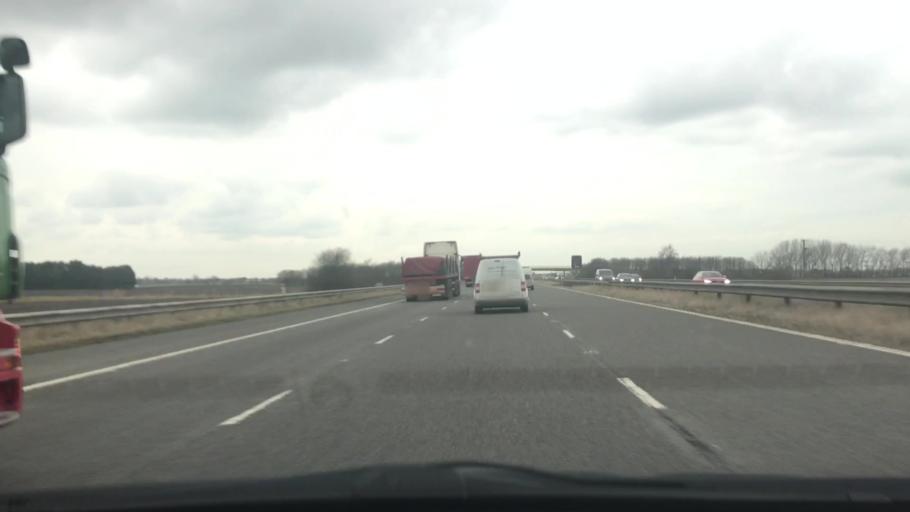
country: GB
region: England
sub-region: Doncaster
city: Hatfield
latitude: 53.5789
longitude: -0.9370
